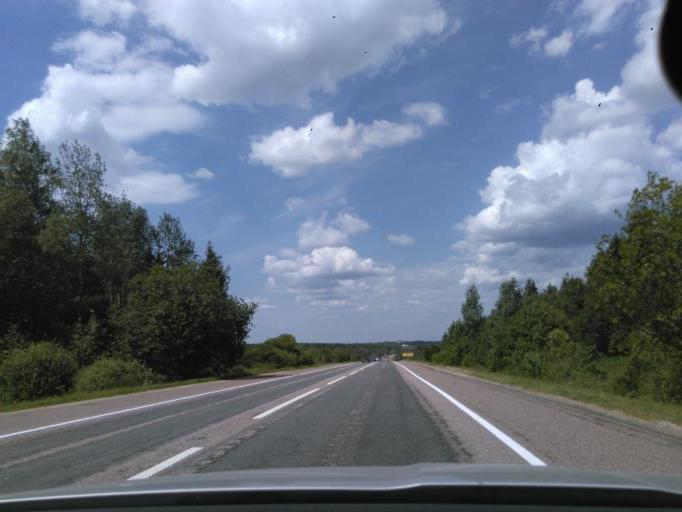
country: RU
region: Moskovskaya
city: Solnechnogorsk
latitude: 56.1421
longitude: 36.9653
